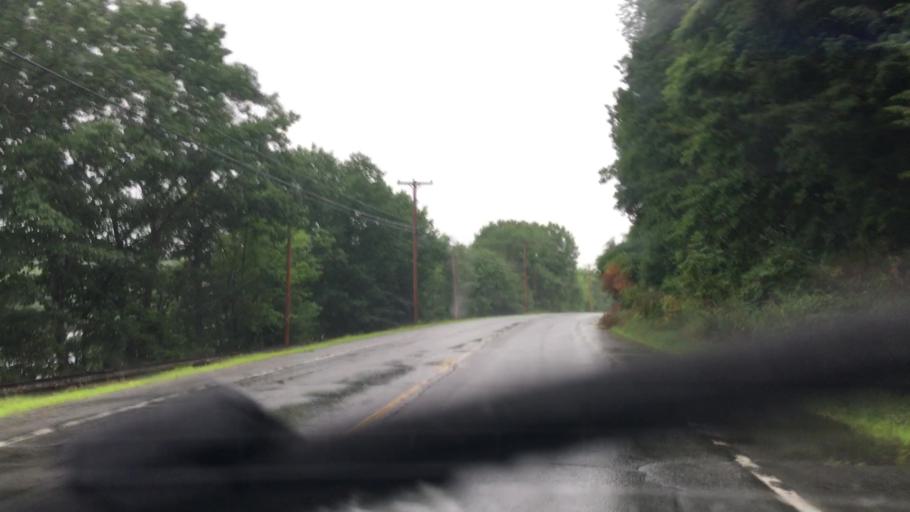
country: US
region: Maine
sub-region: Kennebec County
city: Pittston
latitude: 44.2151
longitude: -69.7626
